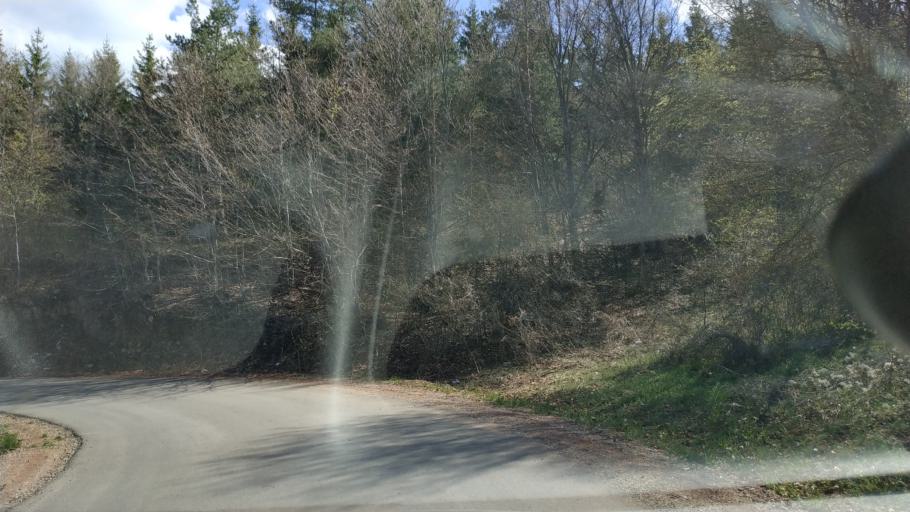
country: RS
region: Central Serbia
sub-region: Zajecarski Okrug
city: Soko Banja
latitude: 43.5816
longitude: 21.8925
